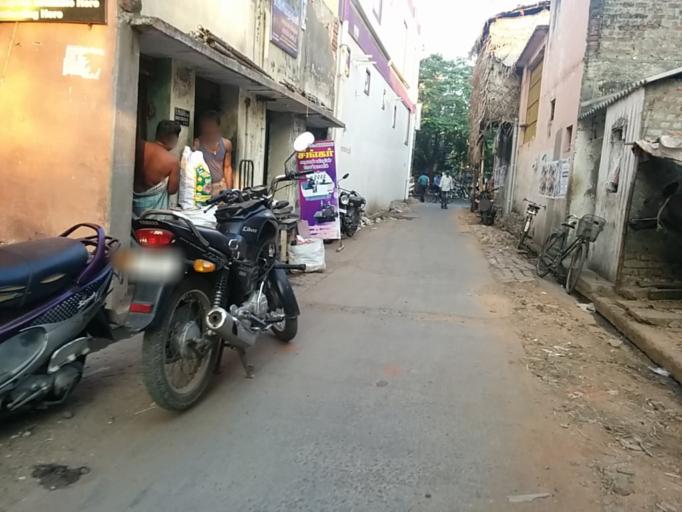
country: IN
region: Pondicherry
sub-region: Puducherry
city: Puducherry
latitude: 11.9382
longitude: 79.8253
